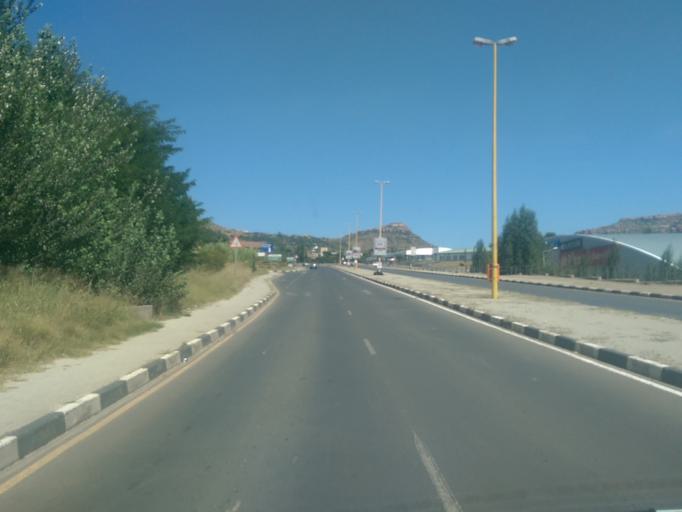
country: LS
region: Maseru
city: Maseru
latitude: -29.3158
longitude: 27.4790
